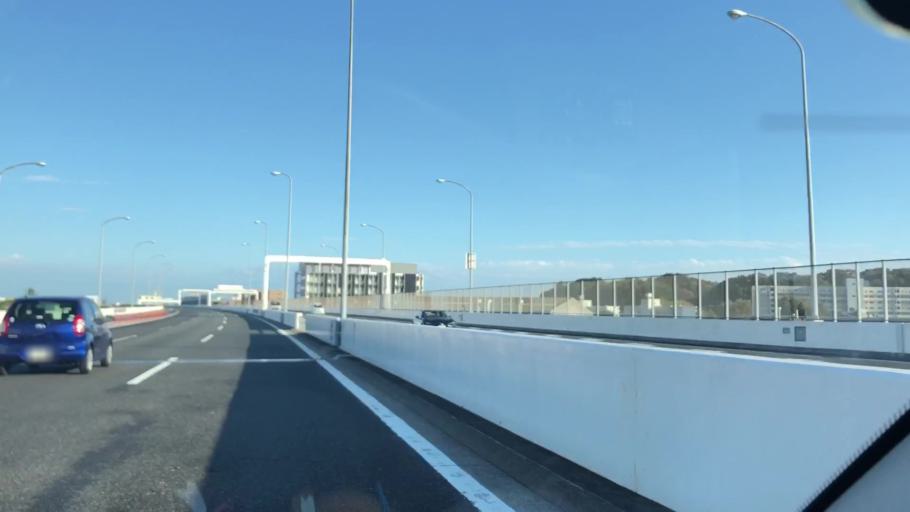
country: JP
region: Kanagawa
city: Yokohama
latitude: 35.3817
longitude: 139.6284
